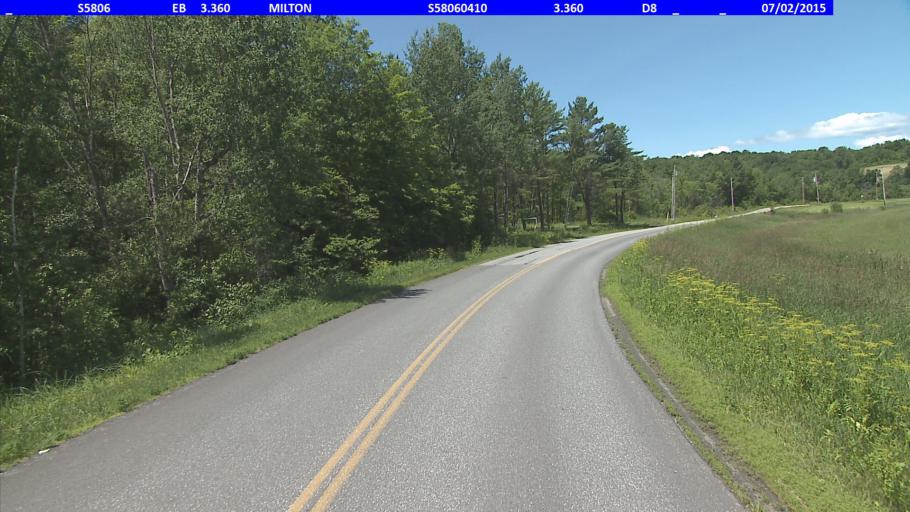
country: US
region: Vermont
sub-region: Chittenden County
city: Milton
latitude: 44.6711
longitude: -73.1729
